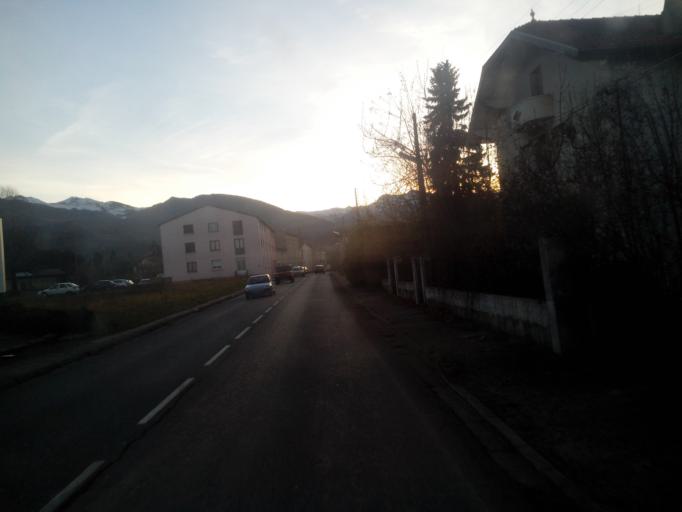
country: FR
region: Midi-Pyrenees
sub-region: Departement de l'Ariege
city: Lavelanet
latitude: 42.9209
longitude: 1.8325
